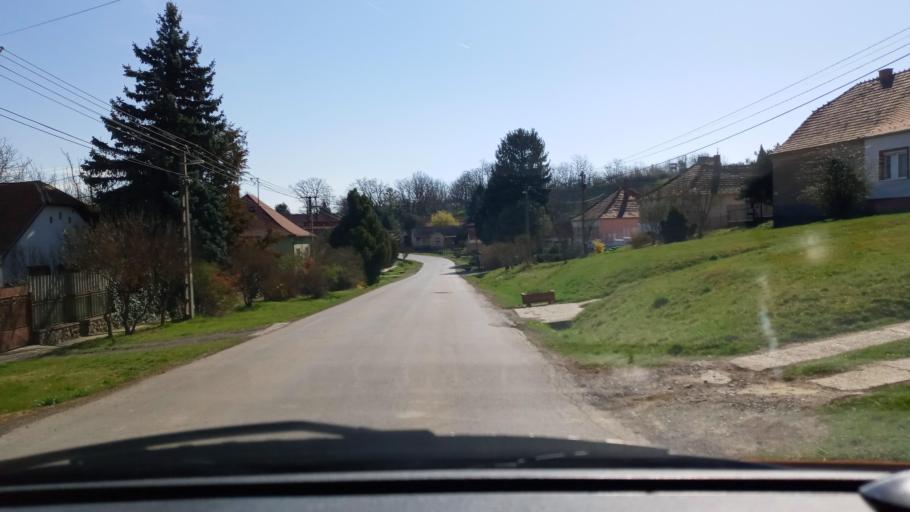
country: HU
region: Baranya
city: Kozarmisleny
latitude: 46.0847
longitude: 18.3157
